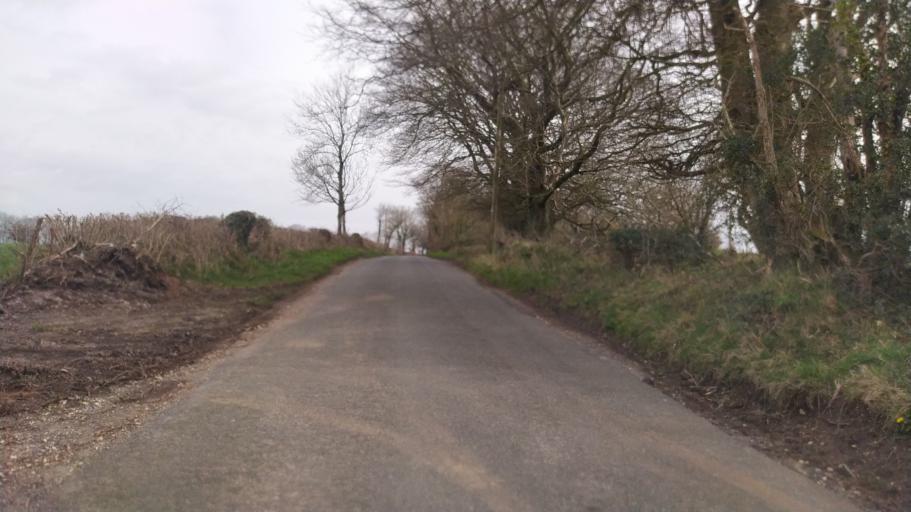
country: GB
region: England
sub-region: Dorset
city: Beaminster
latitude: 50.8324
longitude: -2.7065
